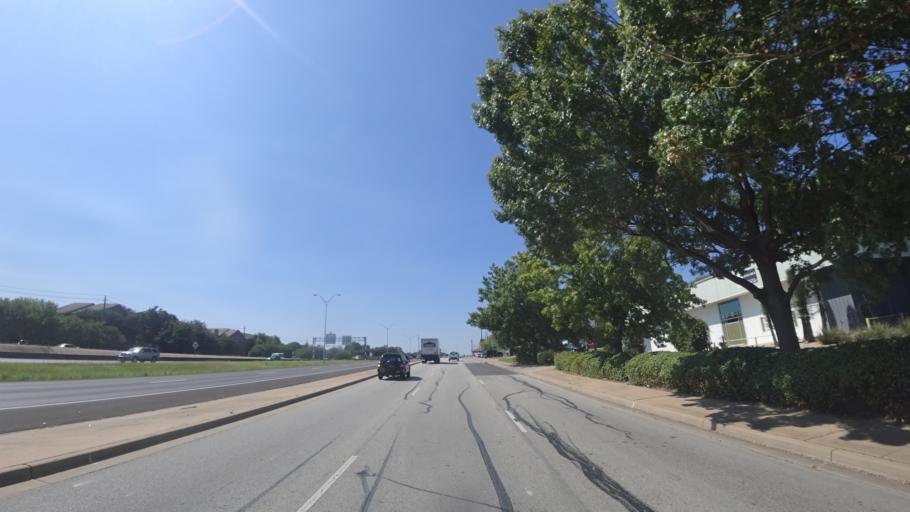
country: US
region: Texas
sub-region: Travis County
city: Austin
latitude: 30.3233
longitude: -97.6808
